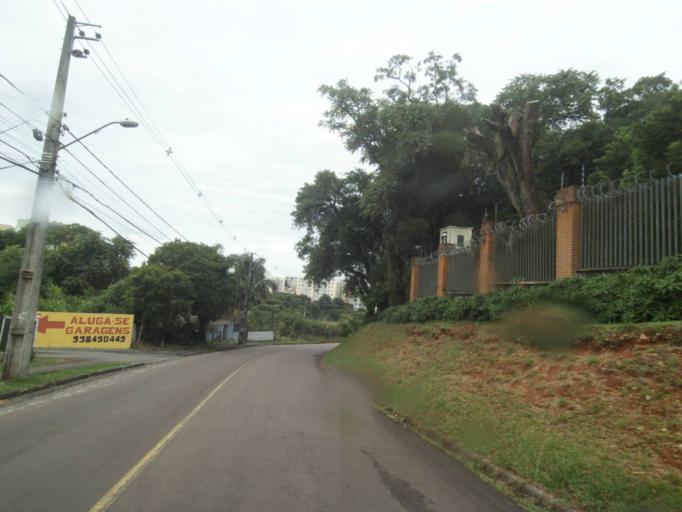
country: BR
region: Parana
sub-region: Curitiba
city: Curitiba
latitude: -25.4595
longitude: -49.3376
